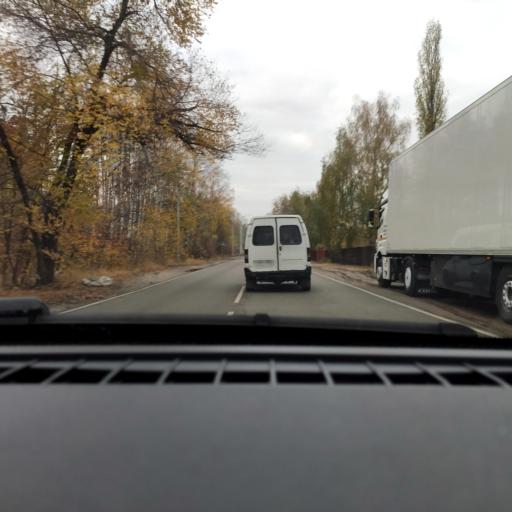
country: RU
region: Voronezj
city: Somovo
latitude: 51.7185
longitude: 39.2944
